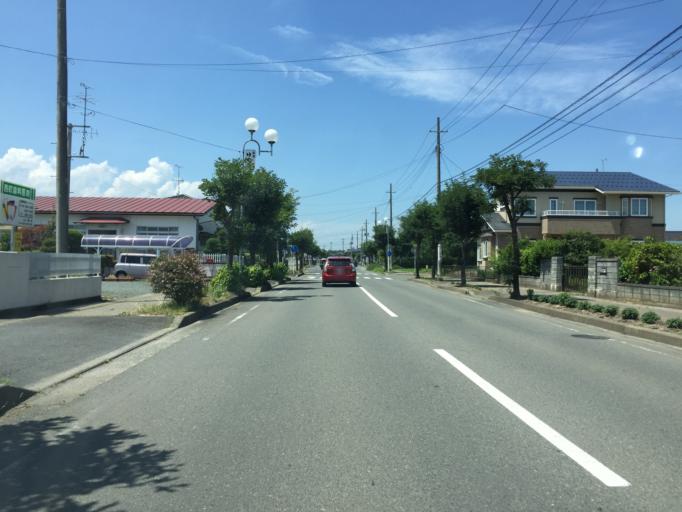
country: JP
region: Fukushima
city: Namie
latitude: 37.7035
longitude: 140.9641
